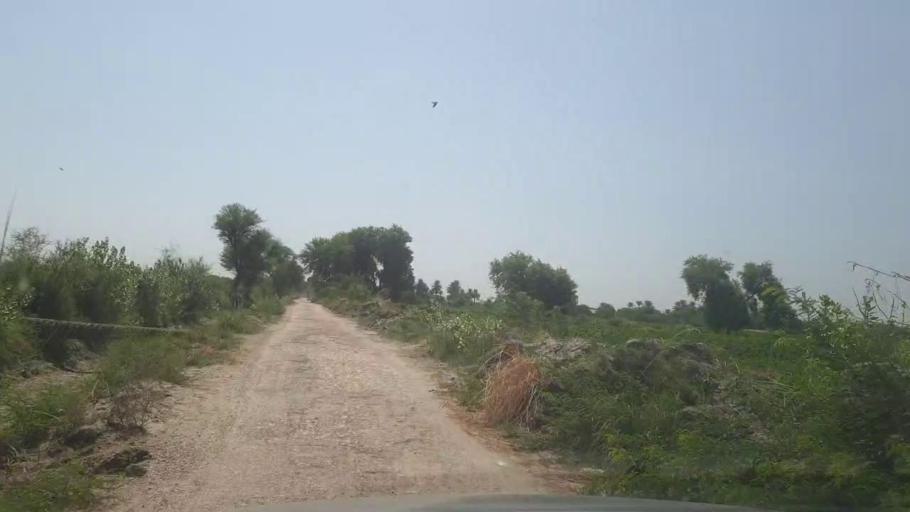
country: PK
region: Sindh
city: Khairpur
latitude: 27.3620
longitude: 69.0299
